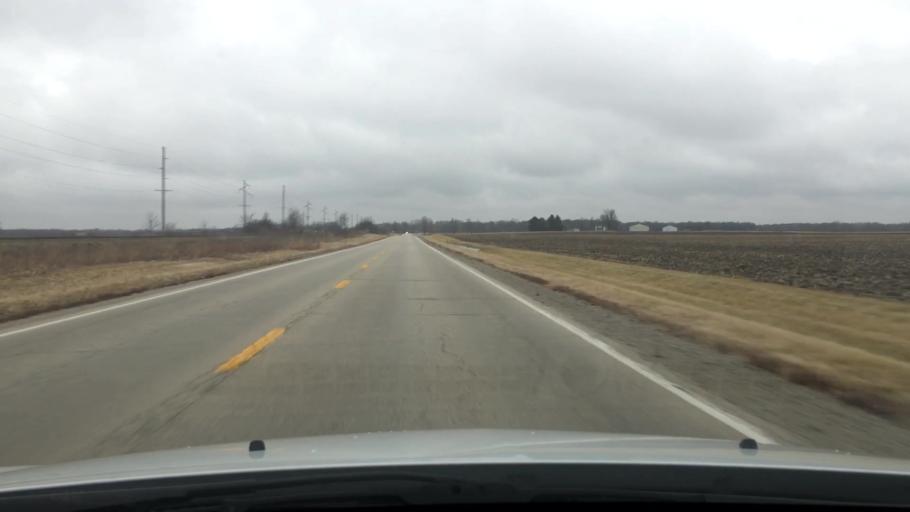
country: US
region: Illinois
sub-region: Iroquois County
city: Sheldon
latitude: 40.8012
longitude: -87.5729
